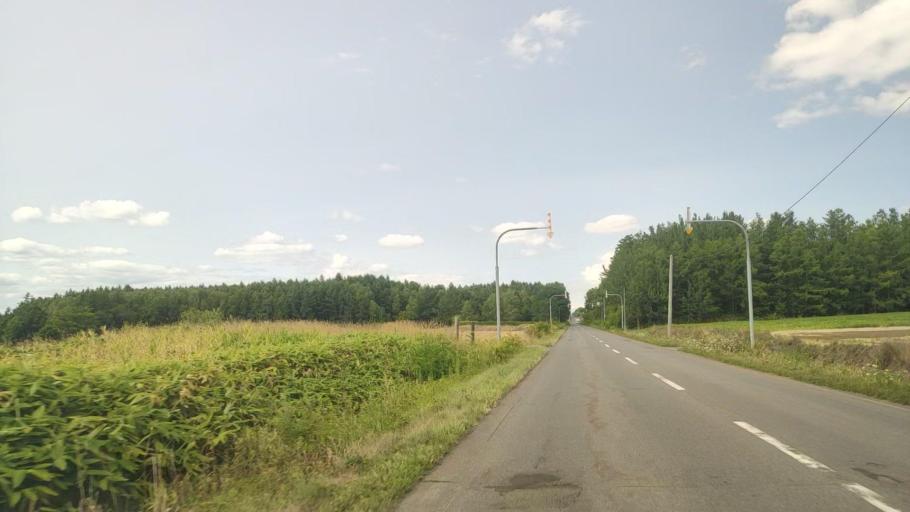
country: JP
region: Hokkaido
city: Nayoro
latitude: 44.2412
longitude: 142.4157
